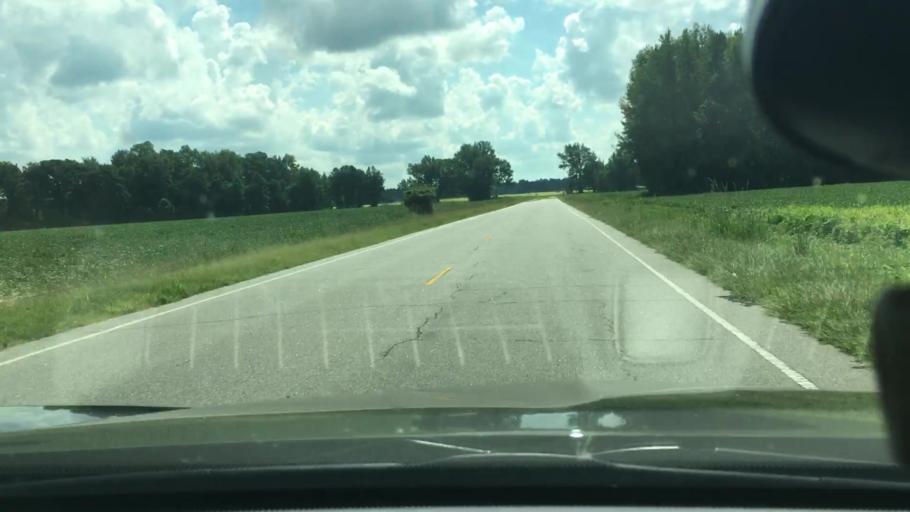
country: US
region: North Carolina
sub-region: Edgecombe County
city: Pinetops
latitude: 35.7562
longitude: -77.5507
